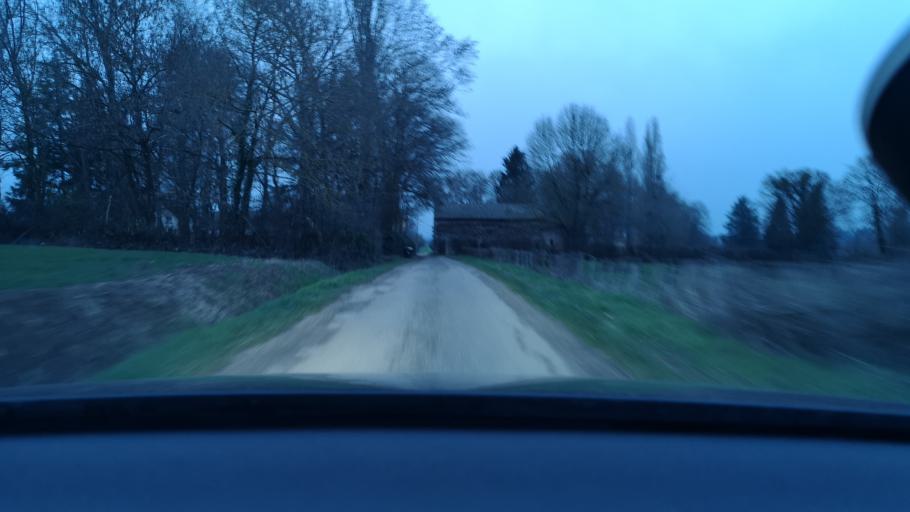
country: FR
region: Bourgogne
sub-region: Departement de Saone-et-Loire
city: Saint-Remy
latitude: 46.7615
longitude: 4.8072
